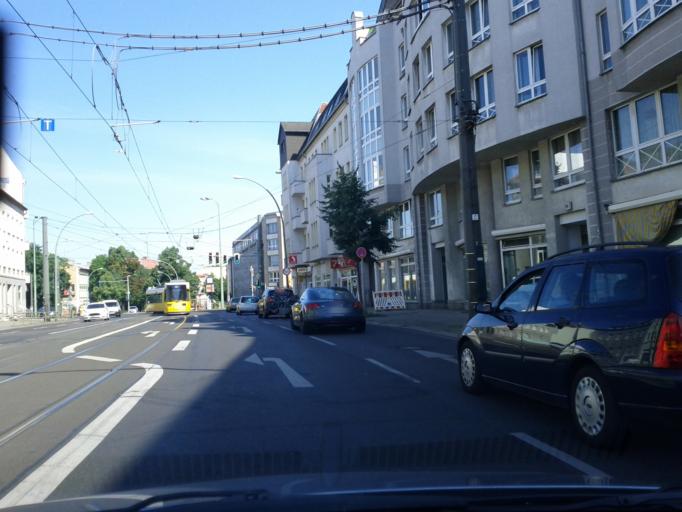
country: DE
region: Berlin
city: Weissensee
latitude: 52.5562
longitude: 13.4674
